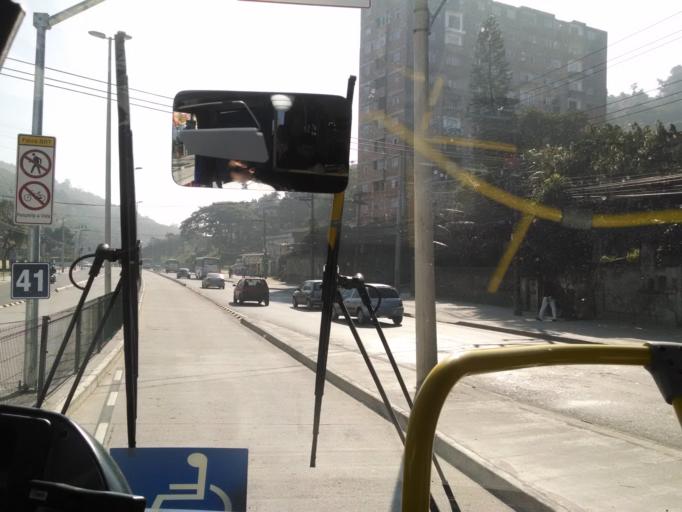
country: BR
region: Rio de Janeiro
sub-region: Sao Joao De Meriti
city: Sao Joao de Meriti
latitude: -22.9150
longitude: -43.3610
